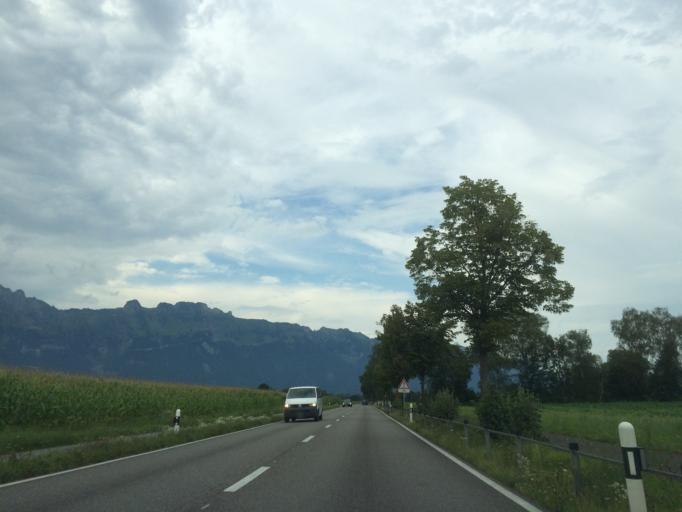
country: LI
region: Schaan
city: Schaan
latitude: 47.1809
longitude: 9.5072
